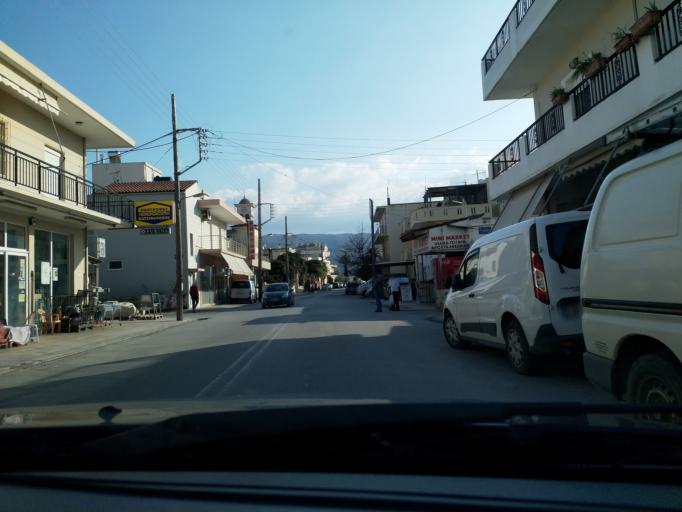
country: GR
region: Crete
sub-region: Nomos Chanias
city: Chania
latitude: 35.5028
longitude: 24.0255
